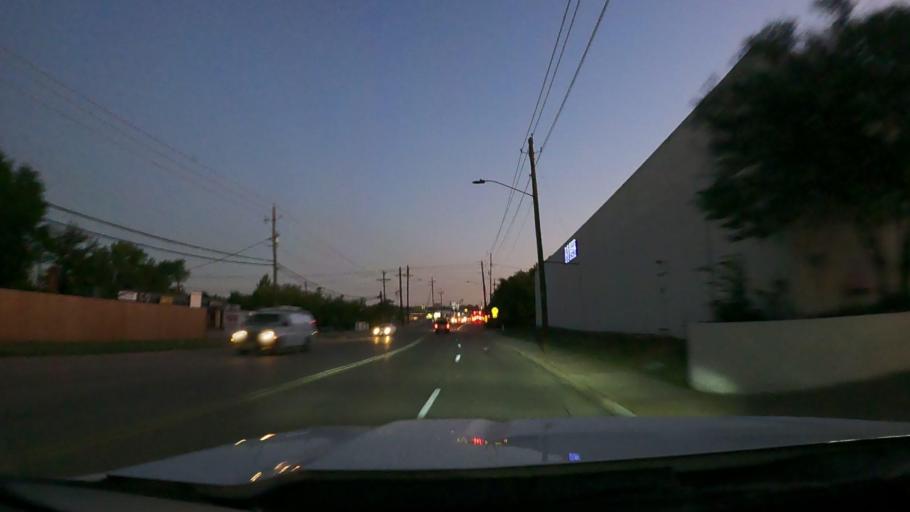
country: US
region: Texas
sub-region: Tarrant County
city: Pantego
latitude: 32.7330
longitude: -97.1492
